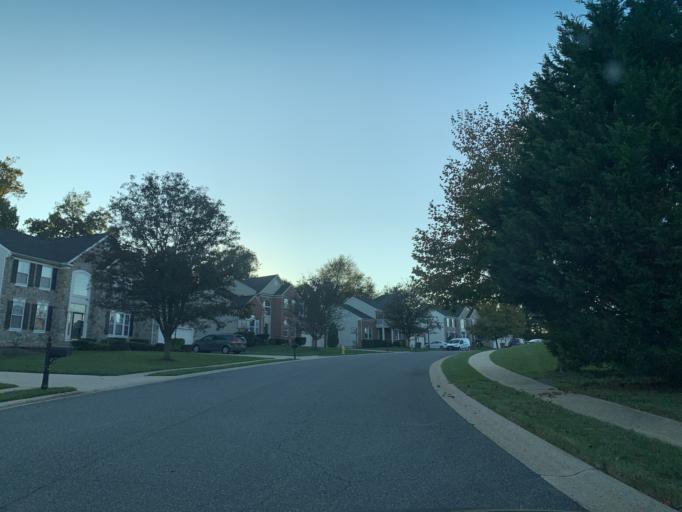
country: US
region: Maryland
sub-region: Harford County
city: Bel Air South
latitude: 39.5261
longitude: -76.2931
